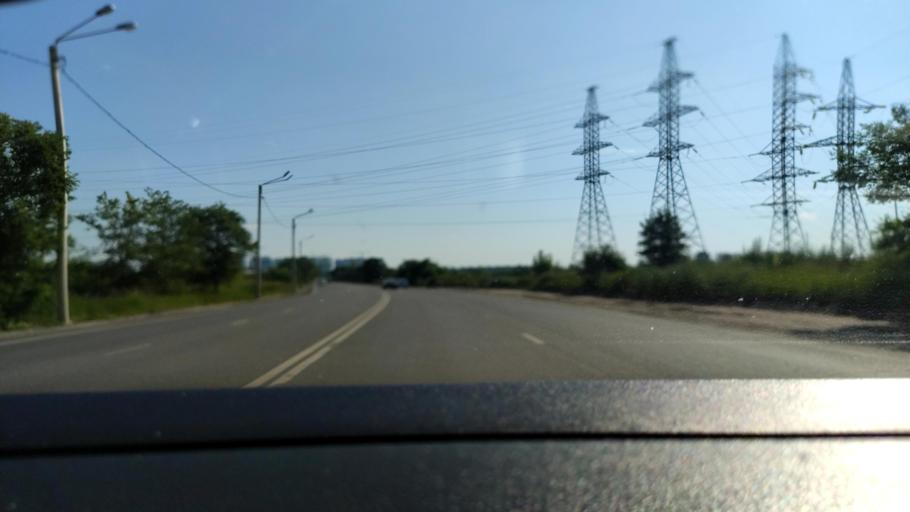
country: RU
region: Voronezj
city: Maslovka
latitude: 51.6203
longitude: 39.2751
